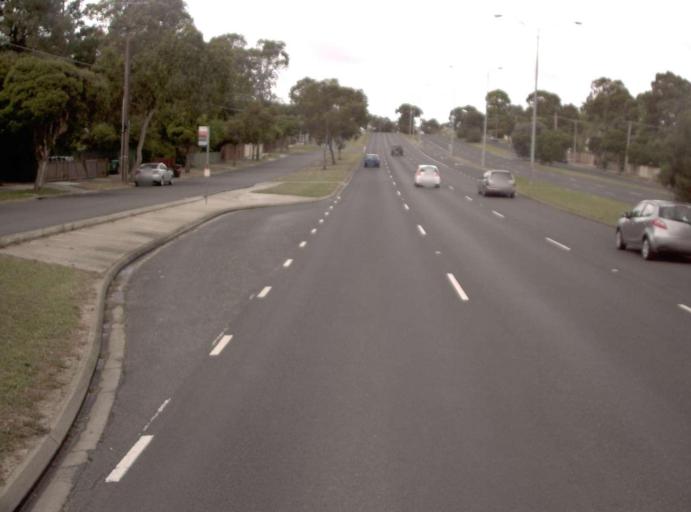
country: AU
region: Victoria
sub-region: Maroondah
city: Croydon North
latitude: -37.7744
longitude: 145.2931
